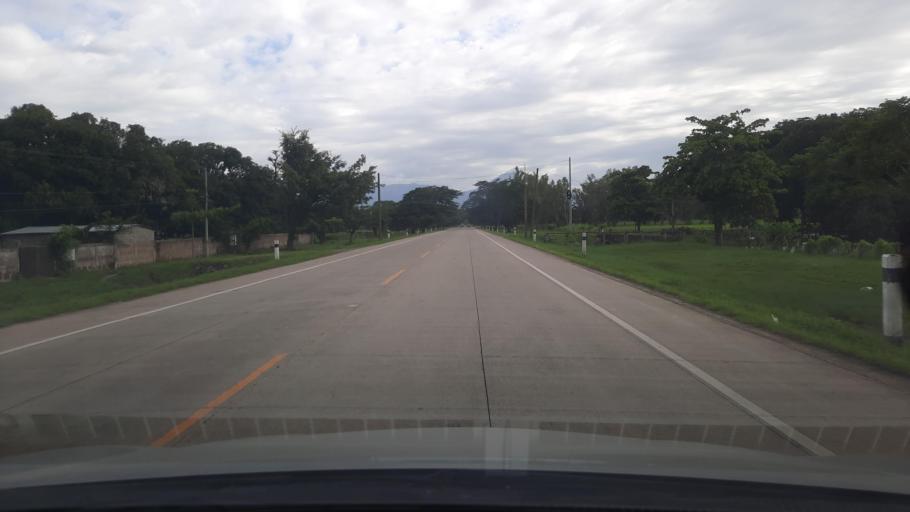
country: NI
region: Chinandega
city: Somotillo
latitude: 12.8545
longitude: -86.8718
